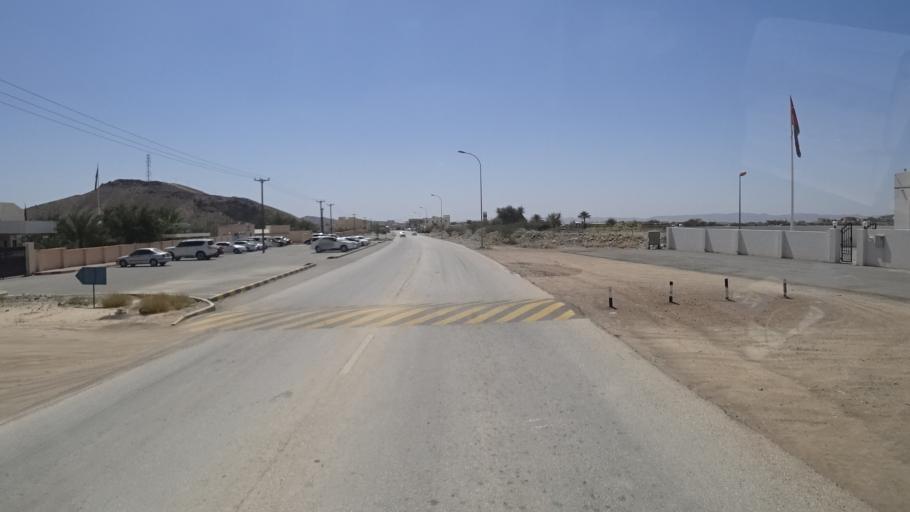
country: OM
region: Az Zahirah
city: `Ibri
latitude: 23.1369
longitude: 56.8920
